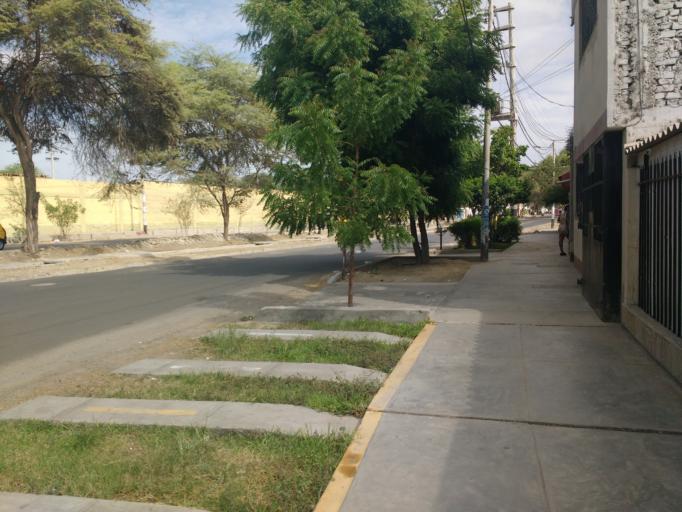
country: PE
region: Piura
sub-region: Provincia de Piura
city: Piura
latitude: -5.1886
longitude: -80.6487
